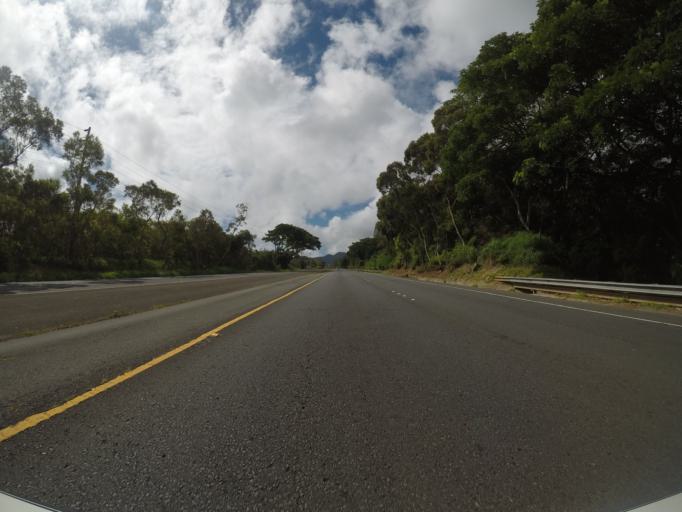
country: US
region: Hawaii
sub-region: Honolulu County
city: Waimanalo
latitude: 21.3644
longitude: -157.7378
